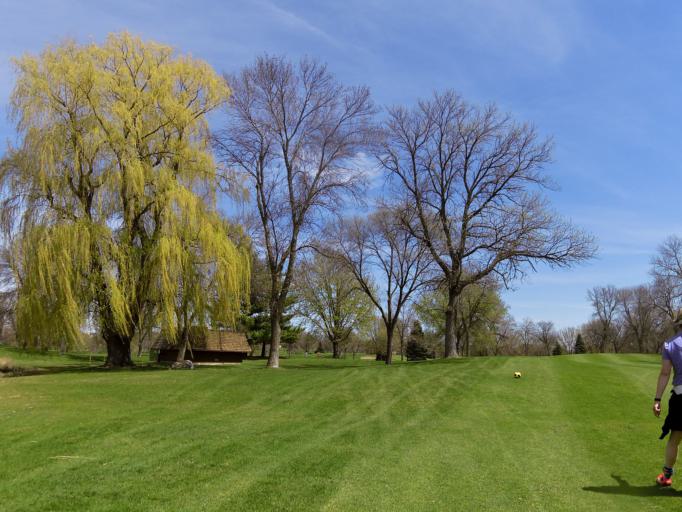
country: US
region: Minnesota
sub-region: Scott County
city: Savage
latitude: 44.8190
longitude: -93.3575
